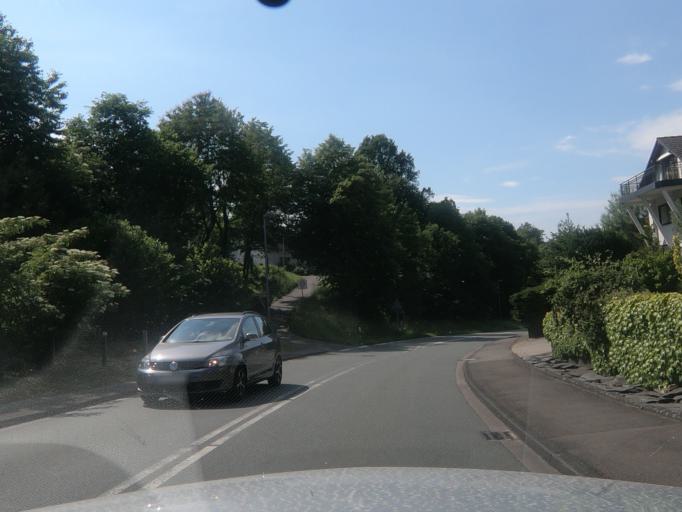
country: DE
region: North Rhine-Westphalia
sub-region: Regierungsbezirk Arnsberg
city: Finnentrop
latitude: 51.1308
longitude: 7.9894
